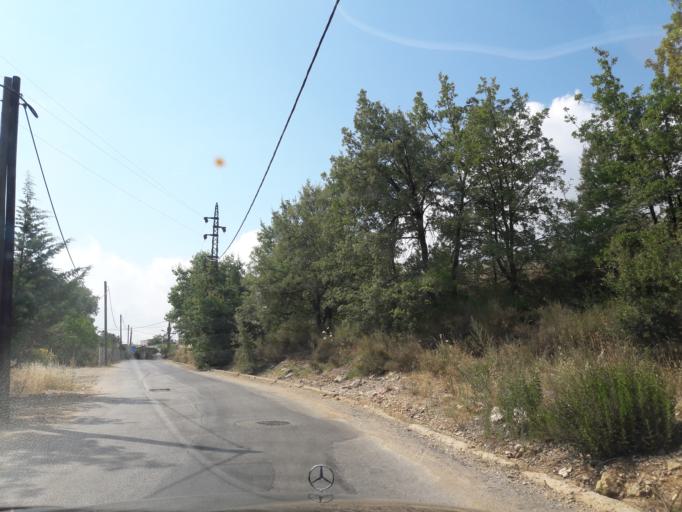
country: LB
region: Mont-Liban
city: Djounie
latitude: 33.9545
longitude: 35.7769
